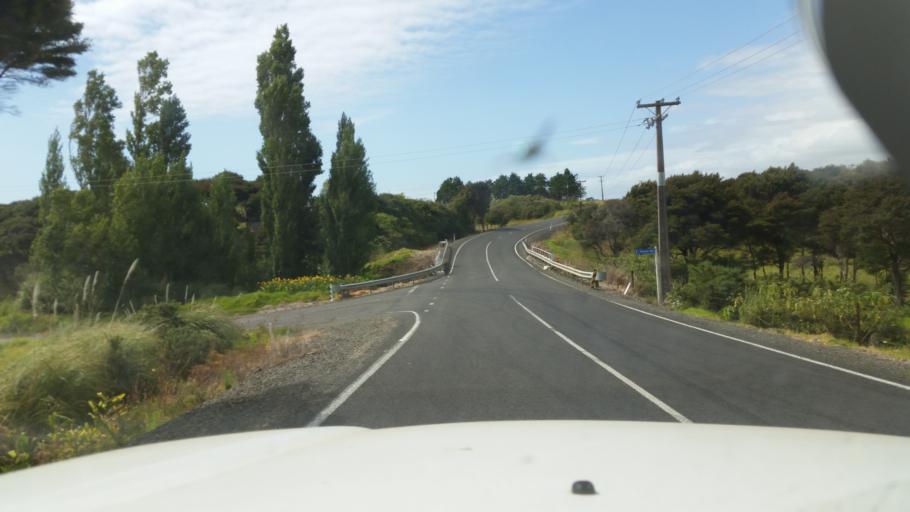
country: NZ
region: Northland
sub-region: Far North District
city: Ahipara
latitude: -35.1828
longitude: 173.1681
